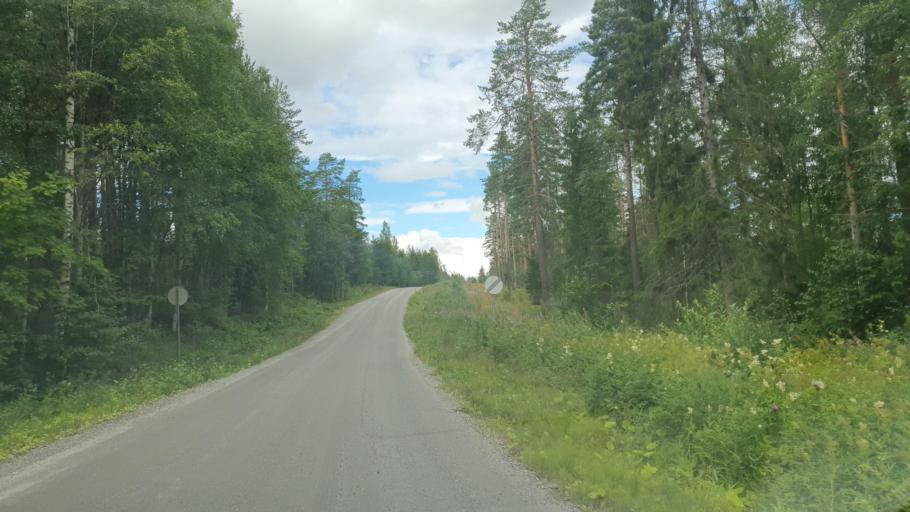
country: FI
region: Kainuu
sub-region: Kehys-Kainuu
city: Kuhmo
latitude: 64.0951
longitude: 29.4170
